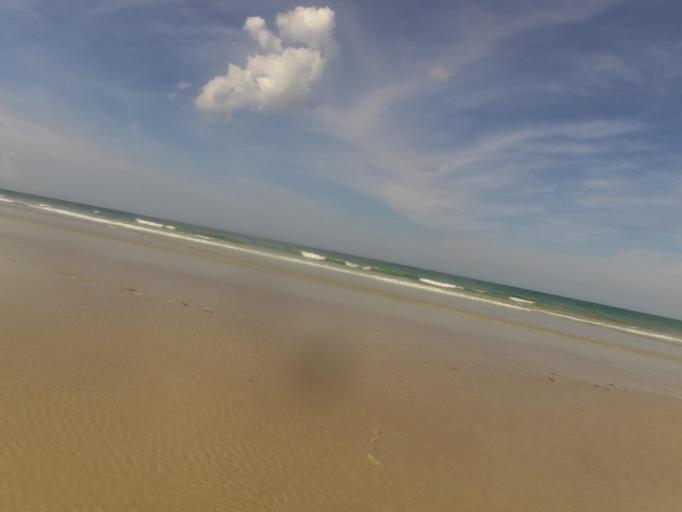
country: US
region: Florida
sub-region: Volusia County
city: Ponce Inlet
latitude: 29.0888
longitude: -80.9274
